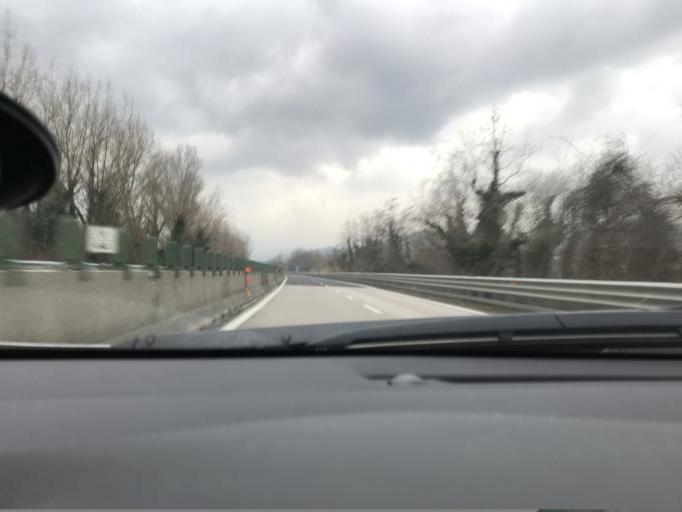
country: IT
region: The Marches
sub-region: Provincia di Ancona
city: Maiolati Spontini
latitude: 43.4926
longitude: 13.1076
